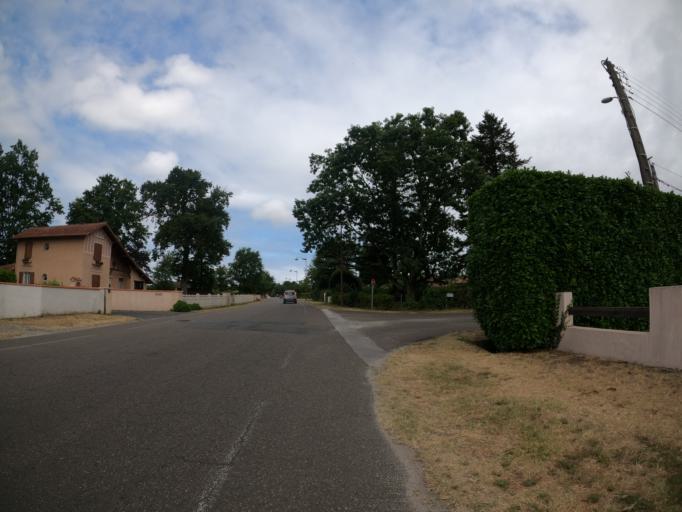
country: FR
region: Aquitaine
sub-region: Departement des Landes
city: Leon
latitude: 43.8814
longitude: -1.3060
